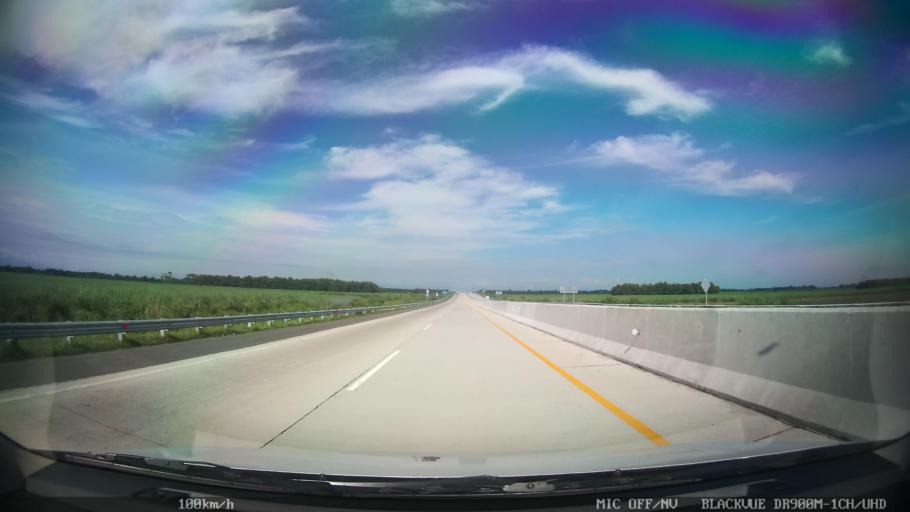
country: ID
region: North Sumatra
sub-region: Kabupaten Langkat
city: Stabat
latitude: 3.7134
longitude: 98.5214
